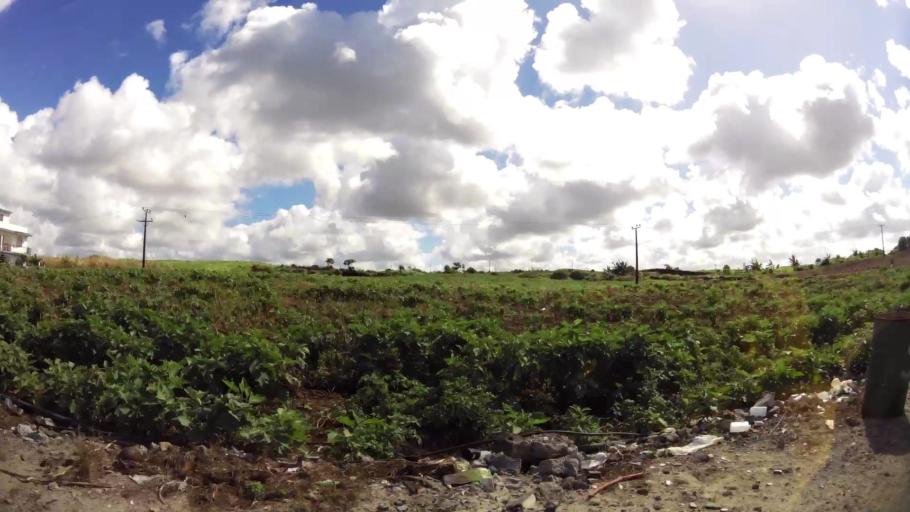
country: MU
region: Grand Port
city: Plaine Magnien
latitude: -20.4278
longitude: 57.6562
